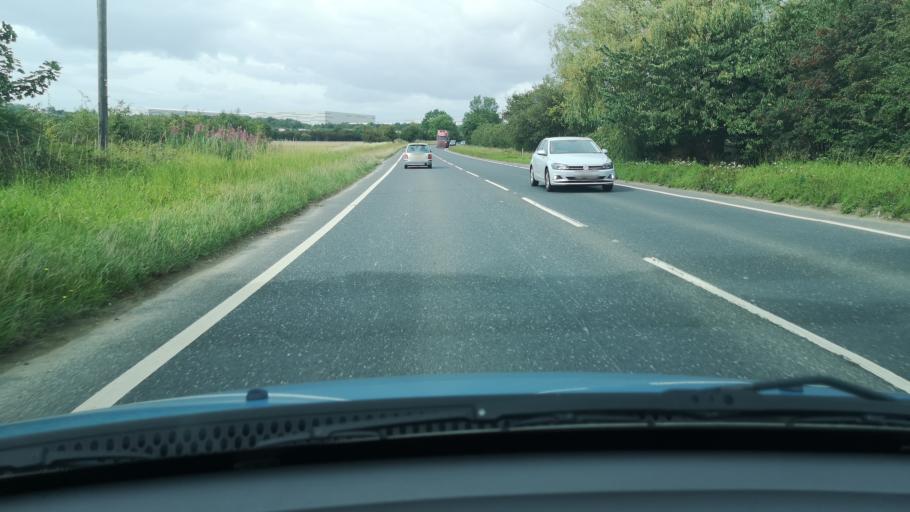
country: GB
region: England
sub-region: City and Borough of Wakefield
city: South Elmsall
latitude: 53.5967
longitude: -1.2539
